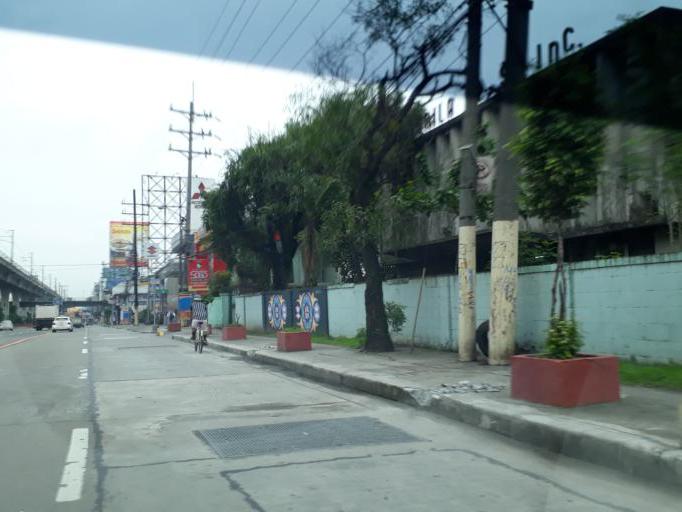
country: PH
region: Calabarzon
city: Del Monte
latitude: 14.6576
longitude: 120.9953
